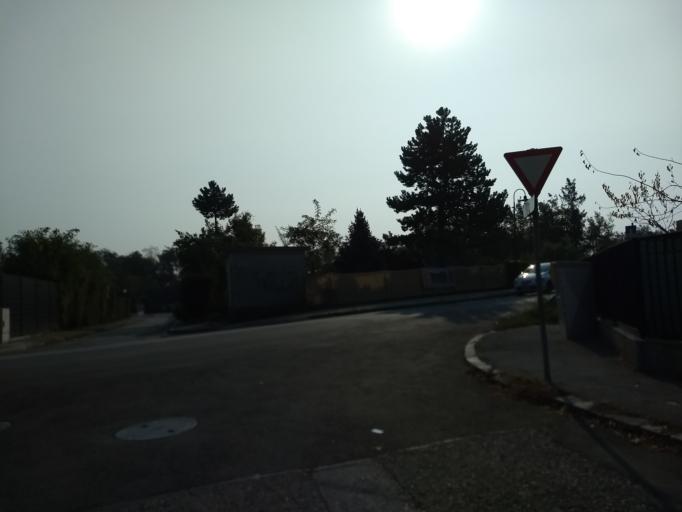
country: AT
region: Lower Austria
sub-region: Politischer Bezirk Modling
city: Brunn am Gebirge
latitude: 48.1196
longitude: 16.2992
